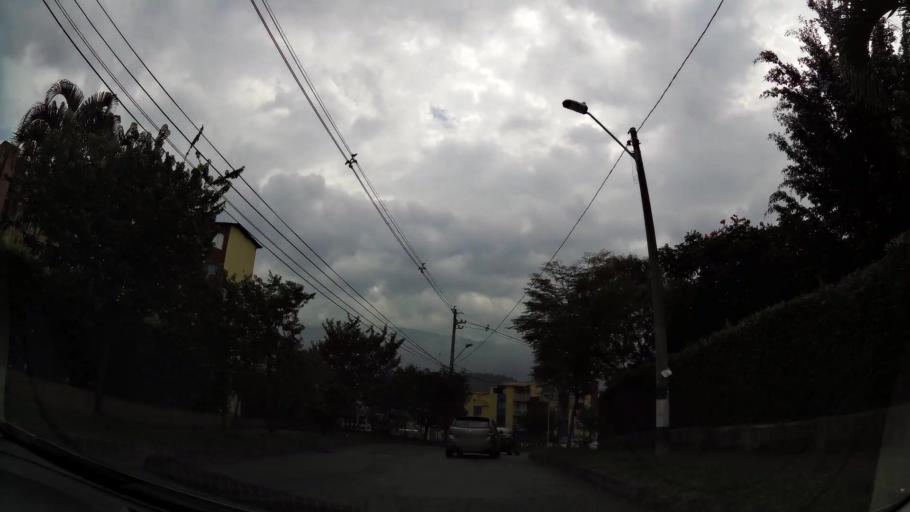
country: CO
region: Antioquia
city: Medellin
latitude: 6.2699
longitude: -75.6009
